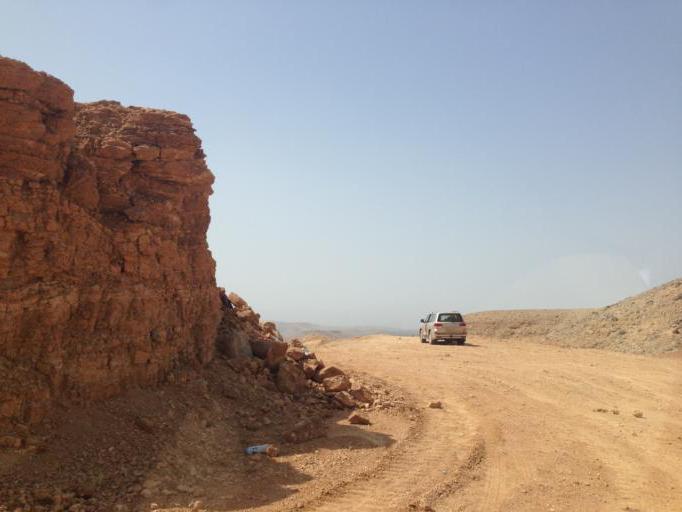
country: OM
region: Ash Sharqiyah
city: Ibra'
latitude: 23.0753
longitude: 58.8879
